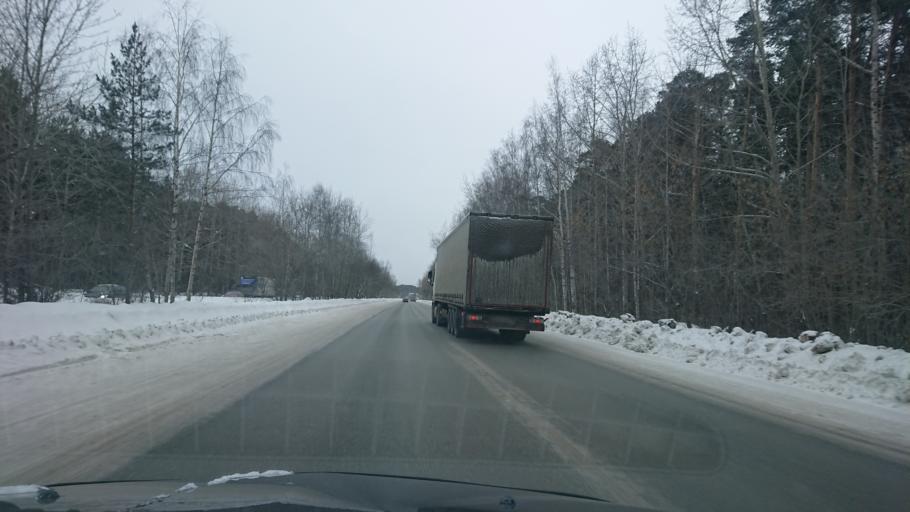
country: RU
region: Sverdlovsk
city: Shirokaya Rechka
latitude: 56.8081
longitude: 60.5295
